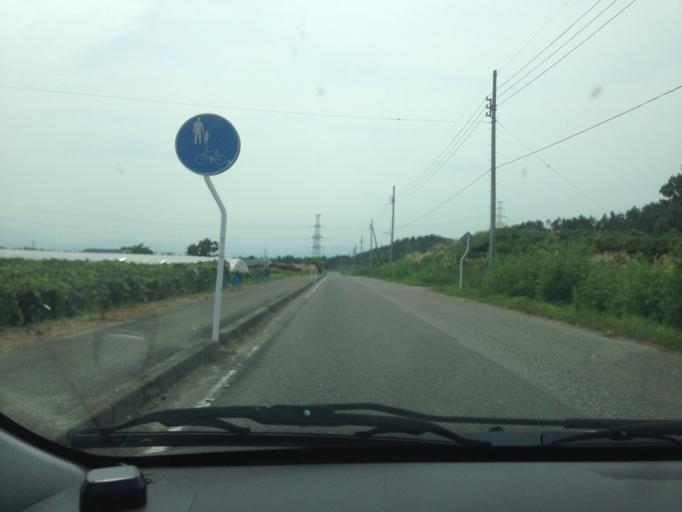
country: JP
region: Fukushima
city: Kitakata
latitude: 37.7148
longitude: 139.8706
